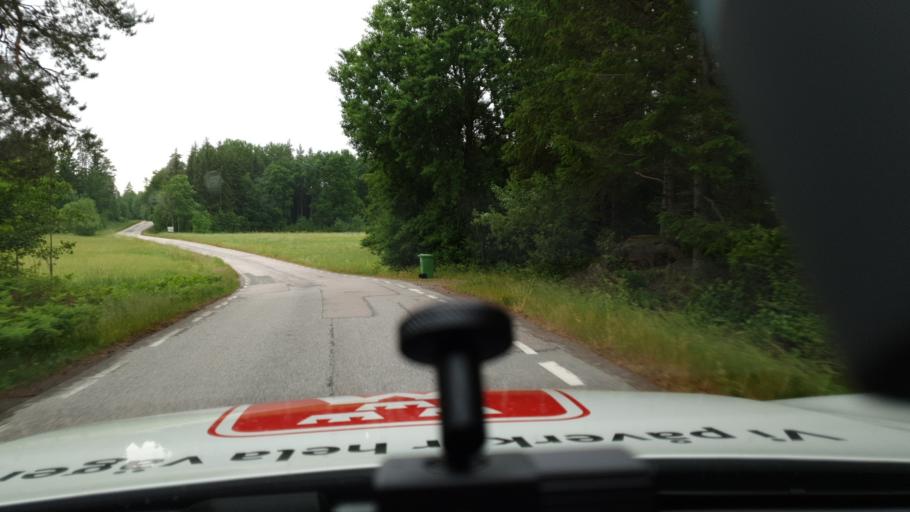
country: SE
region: Vaestra Goetaland
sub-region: Toreboda Kommun
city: Toereboda
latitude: 58.8266
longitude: 14.0043
